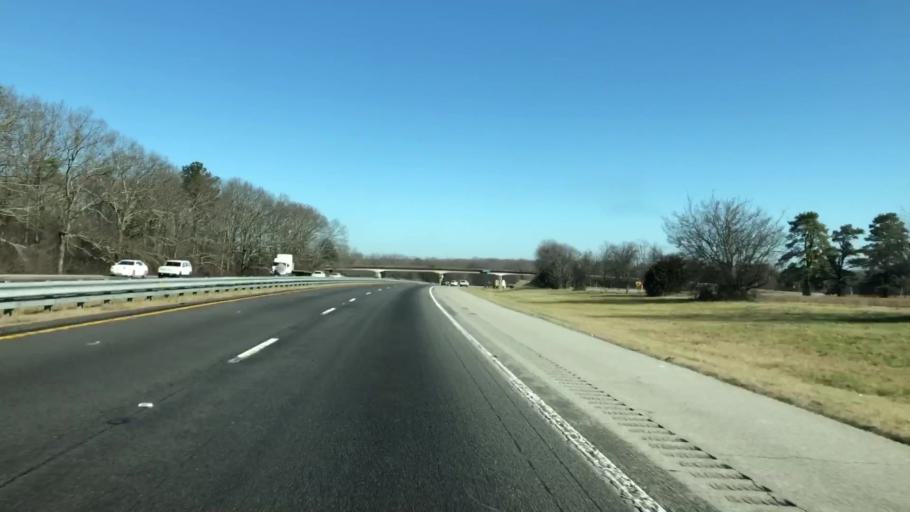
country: US
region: Alabama
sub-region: Limestone County
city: Athens
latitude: 34.8885
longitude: -86.9164
